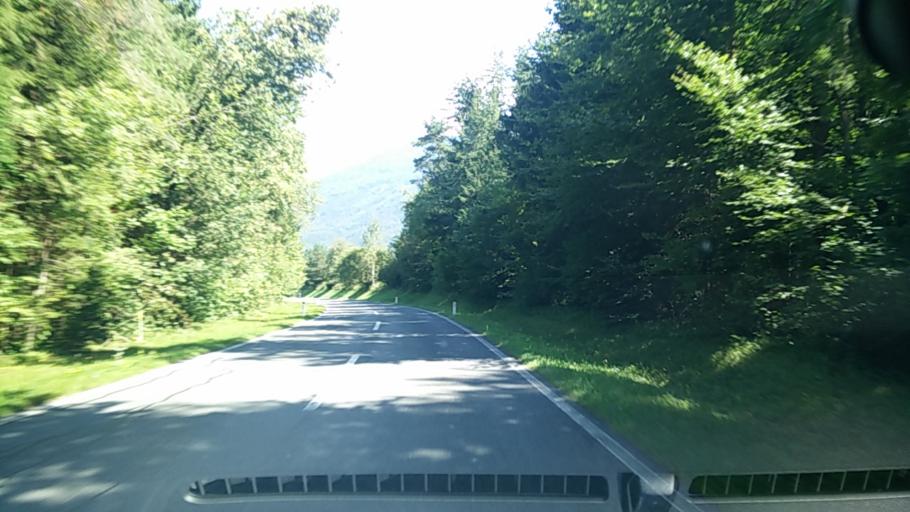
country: AT
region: Carinthia
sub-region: Politischer Bezirk Volkermarkt
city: Sittersdorf
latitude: 46.5399
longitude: 14.5653
